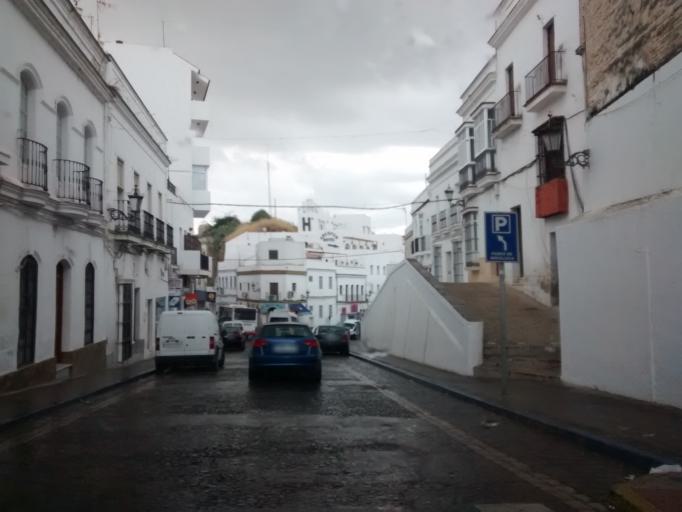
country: ES
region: Andalusia
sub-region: Provincia de Cadiz
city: Arcos de la Frontera
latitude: 36.7507
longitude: -5.8113
